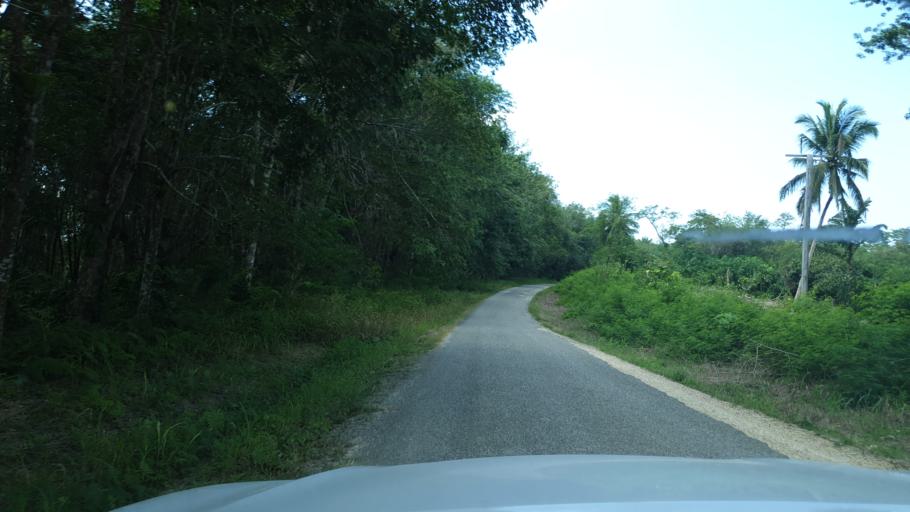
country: PG
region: East Sepik
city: Angoram
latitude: -3.9596
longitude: 144.0354
